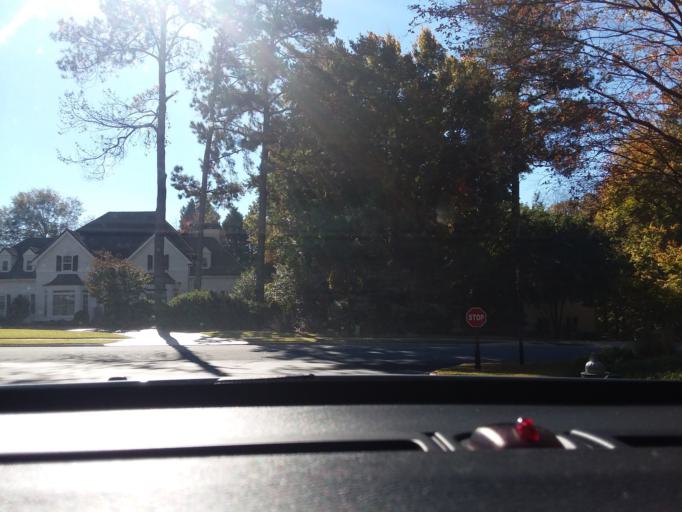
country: US
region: Georgia
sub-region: Fulton County
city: Johns Creek
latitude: 34.0222
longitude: -84.1827
